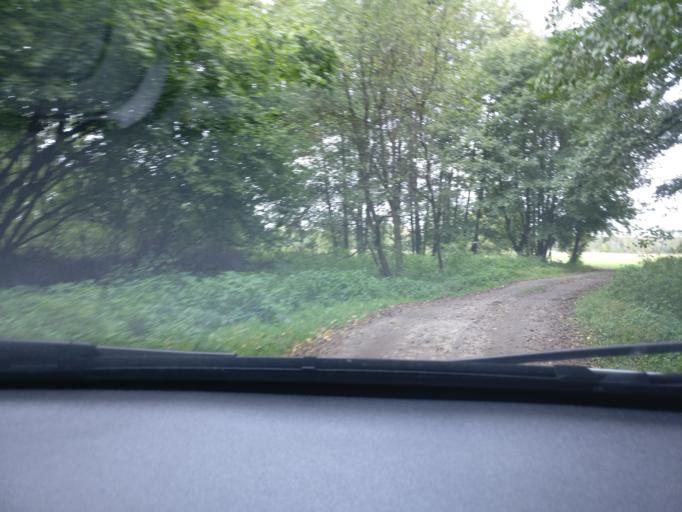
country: PL
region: Masovian Voivodeship
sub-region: Powiat kozienicki
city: Garbatka-Letnisko
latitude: 51.5166
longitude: 21.5983
